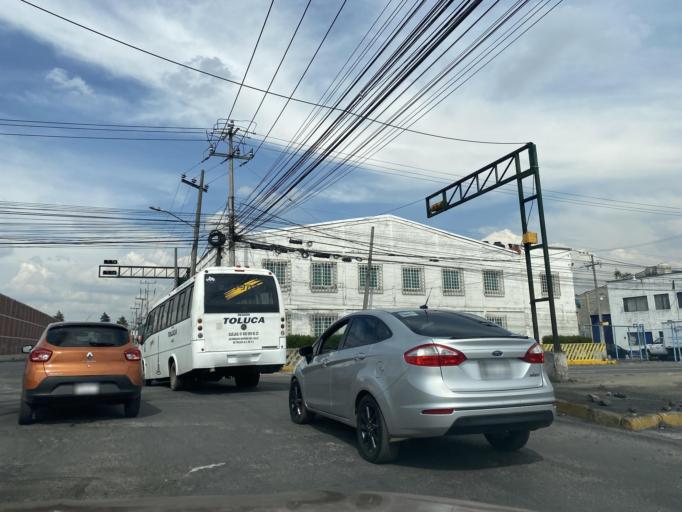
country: IN
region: Karnataka
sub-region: Dakshina Kannada
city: Puttur
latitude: 12.7380
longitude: 75.1833
